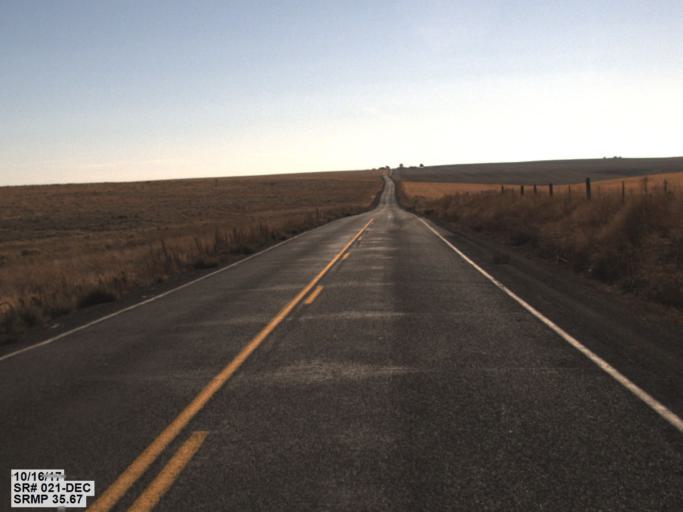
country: US
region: Washington
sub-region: Adams County
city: Ritzville
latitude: 47.0669
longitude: -118.6630
